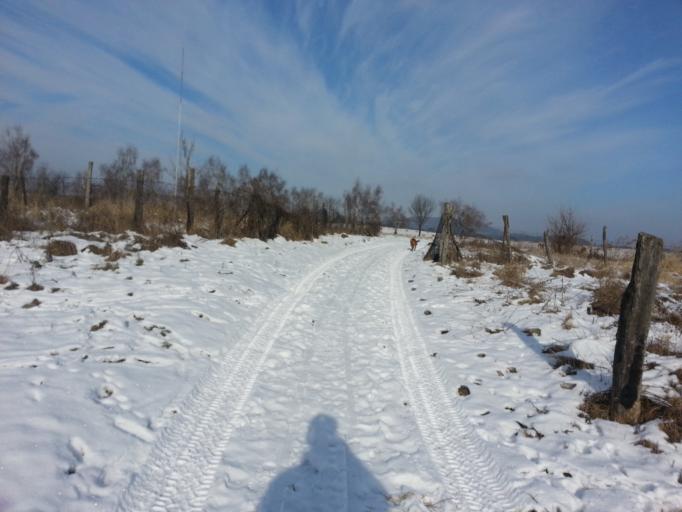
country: HU
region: Nograd
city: Somoskoujfalu
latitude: 48.1290
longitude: 19.8847
